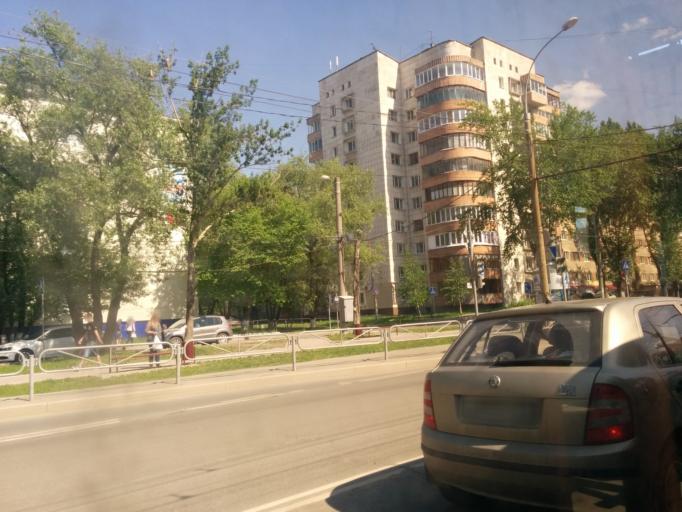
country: RU
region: Perm
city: Perm
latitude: 58.0106
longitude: 56.2808
